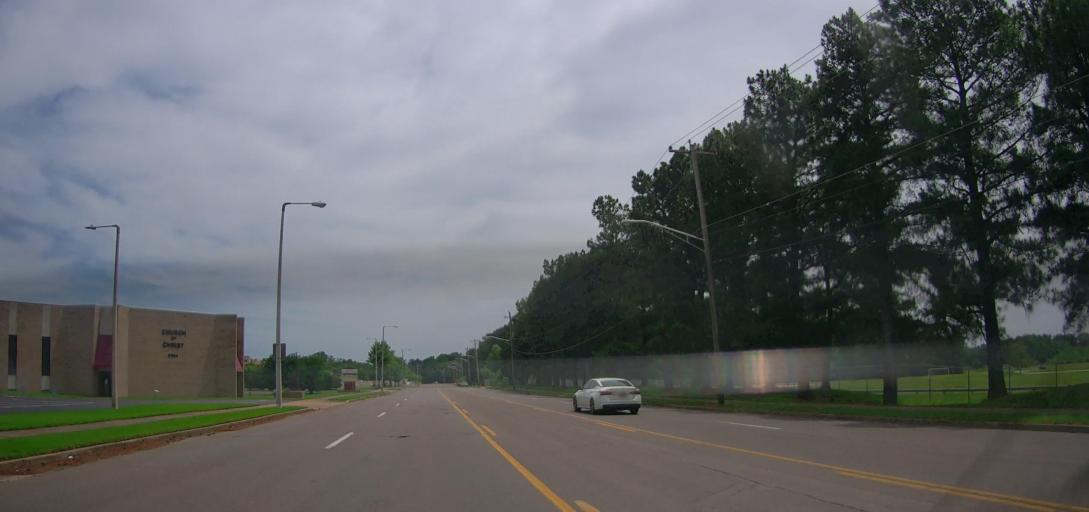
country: US
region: Tennessee
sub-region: Shelby County
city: Germantown
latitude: 35.0768
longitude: -89.8505
